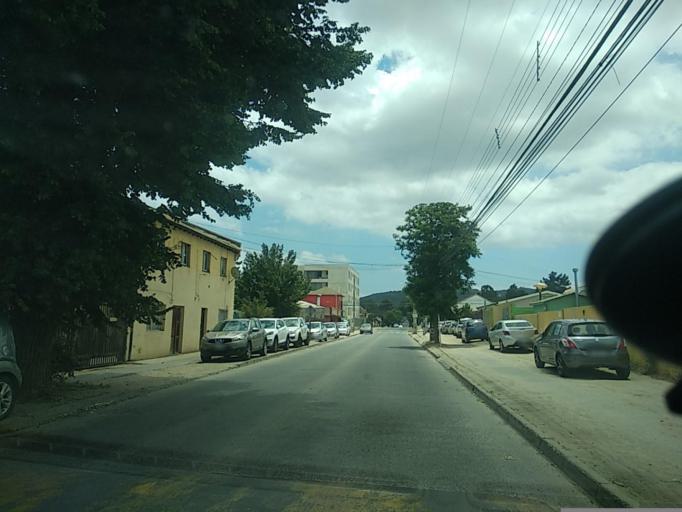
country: CL
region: Valparaiso
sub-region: Provincia de Marga Marga
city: Villa Alemana
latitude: -33.0381
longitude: -71.4055
